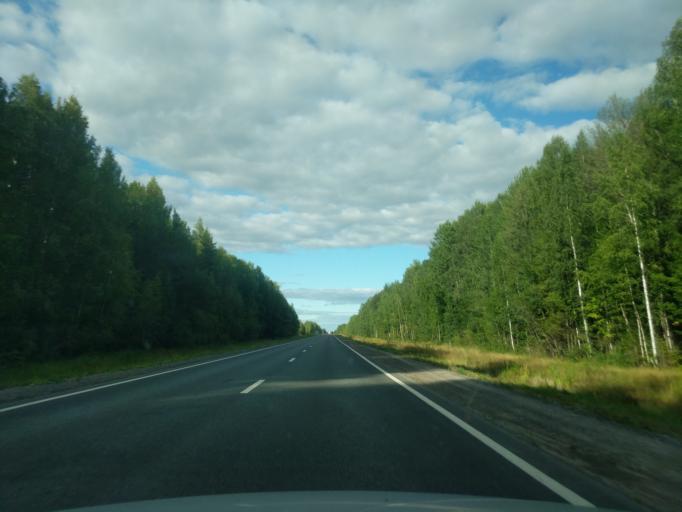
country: RU
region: Kostroma
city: Manturovo
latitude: 58.2249
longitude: 44.6243
